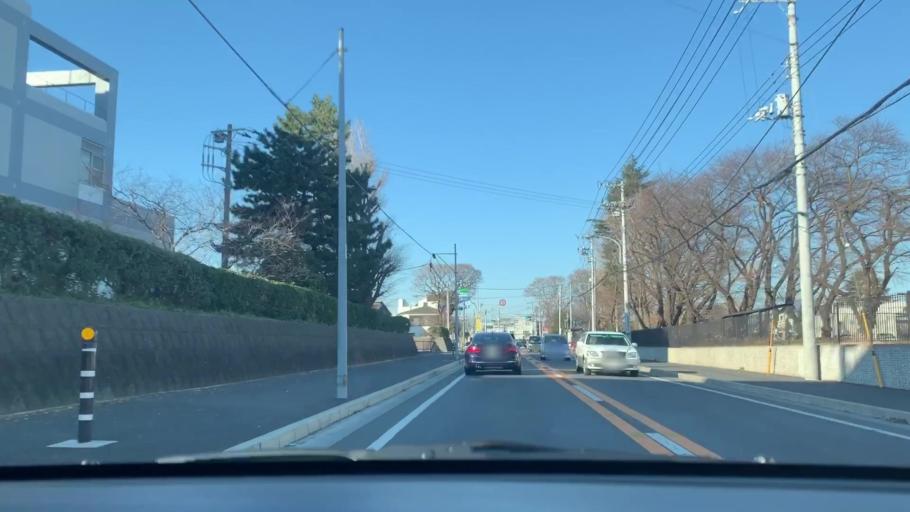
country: JP
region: Chiba
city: Matsudo
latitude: 35.7457
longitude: 139.9050
